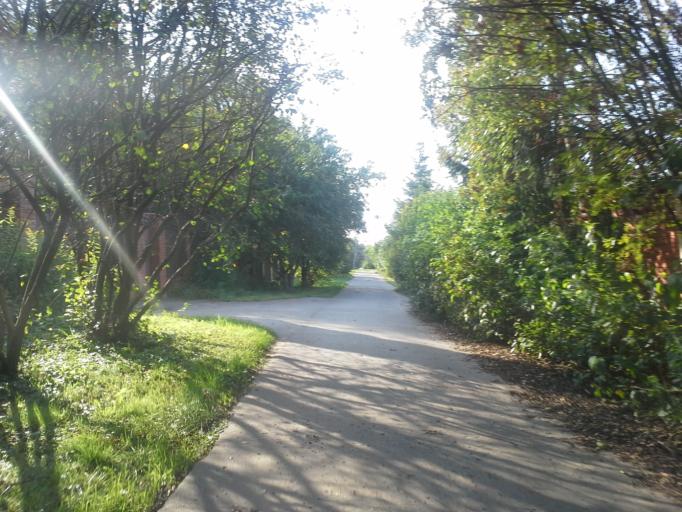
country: RU
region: Moskovskaya
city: Filimonki
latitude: 55.5375
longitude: 37.3592
